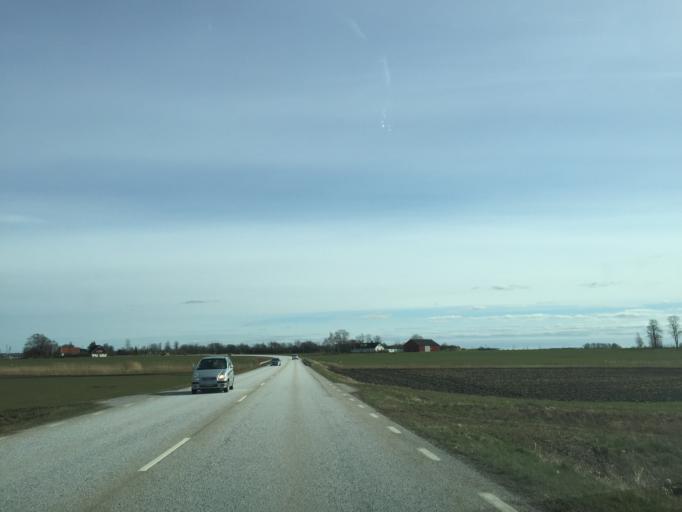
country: SE
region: Skane
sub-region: Lomma Kommun
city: Lomma
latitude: 55.7208
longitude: 13.0663
